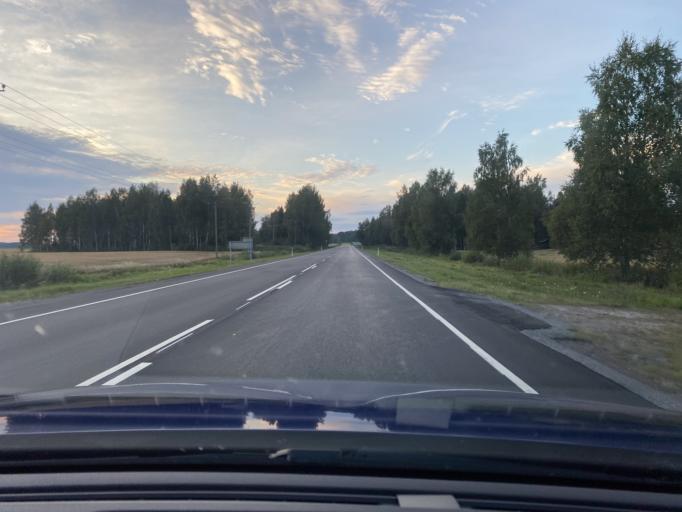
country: FI
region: Satakunta
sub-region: Pohjois-Satakunta
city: Kankaanpaeae
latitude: 61.8342
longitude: 22.3488
